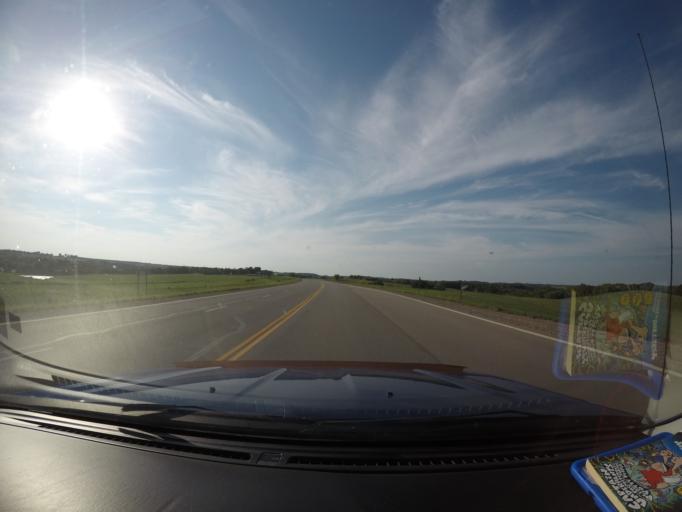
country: US
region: Kansas
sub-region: Atchison County
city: Atchison
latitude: 39.4709
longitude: -95.0973
